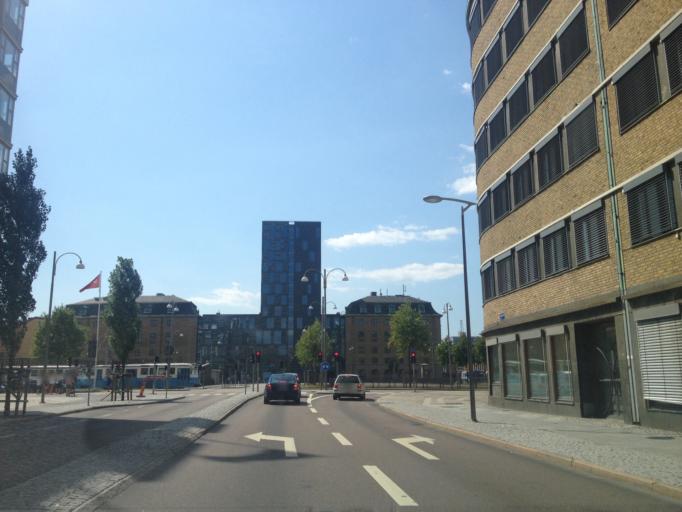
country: SE
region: Vaestra Goetaland
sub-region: Goteborg
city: Goeteborg
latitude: 57.7087
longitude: 11.9785
